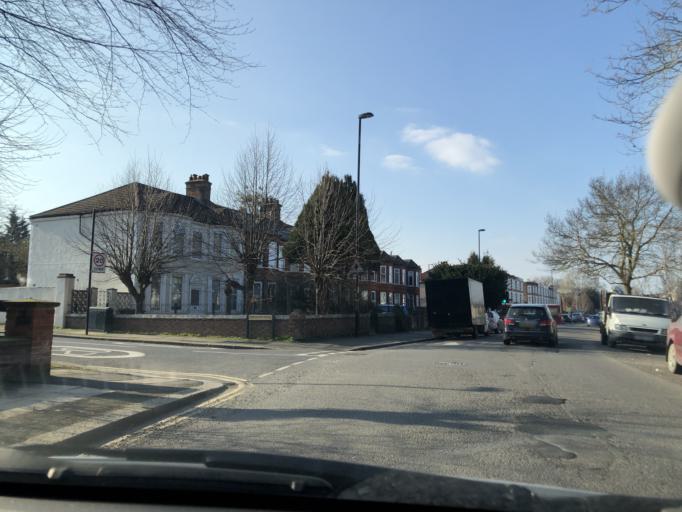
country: GB
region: England
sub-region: Greater London
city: Blackheath
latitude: 51.4466
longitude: 0.0011
